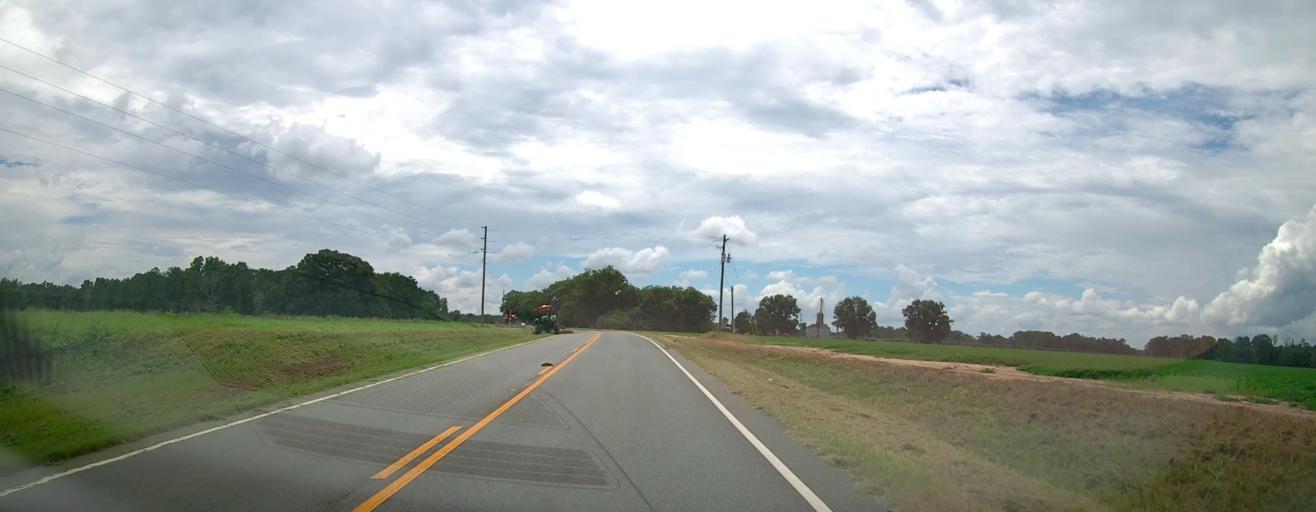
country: US
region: Georgia
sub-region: Macon County
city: Oglethorpe
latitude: 32.2830
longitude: -84.1682
